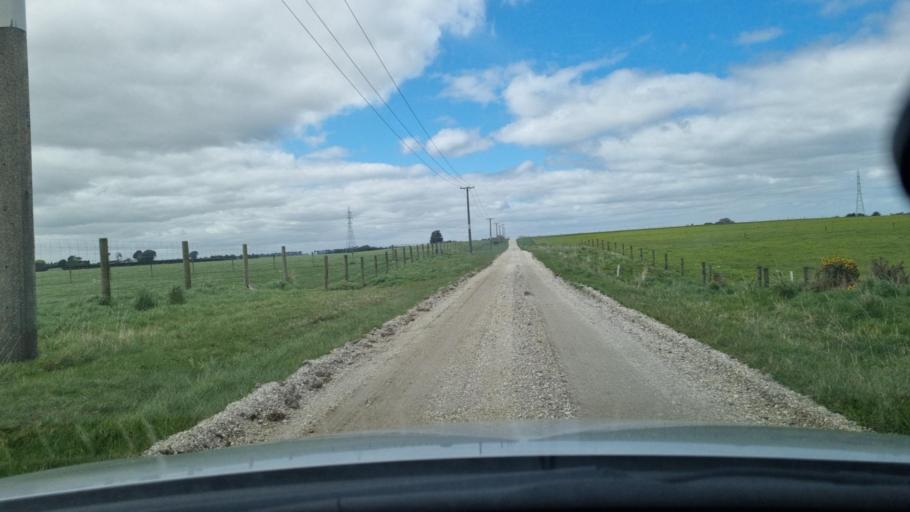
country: NZ
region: Southland
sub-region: Invercargill City
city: Invercargill
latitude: -46.4427
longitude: 168.4438
